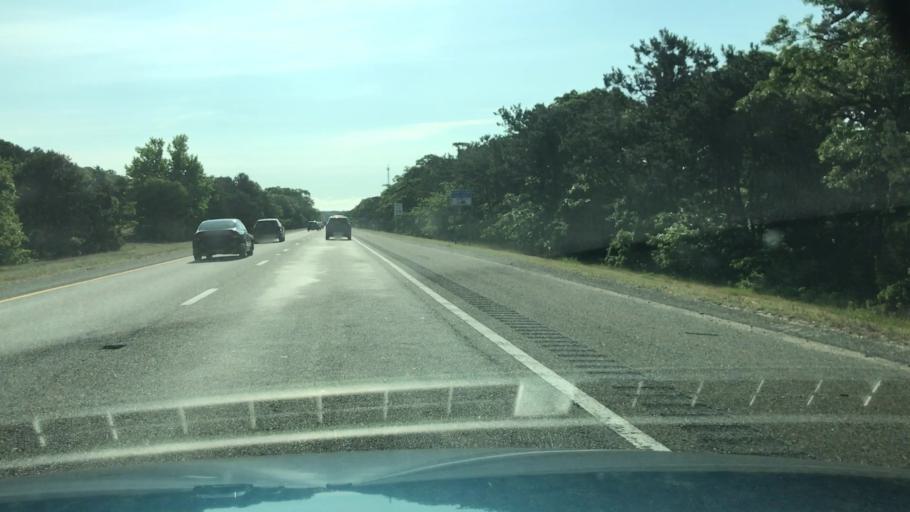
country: US
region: Massachusetts
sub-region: Barnstable County
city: Yarmouth
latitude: 41.6904
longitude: -70.2067
